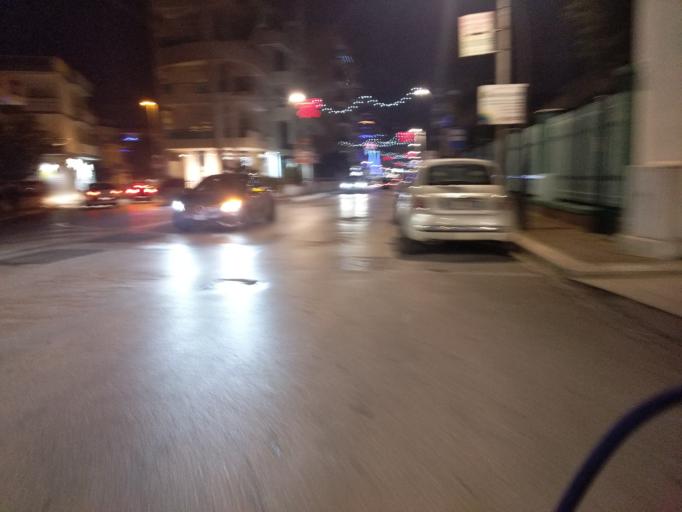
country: IT
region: Apulia
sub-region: Provincia di Bari
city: Modugno
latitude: 41.0859
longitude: 16.7864
